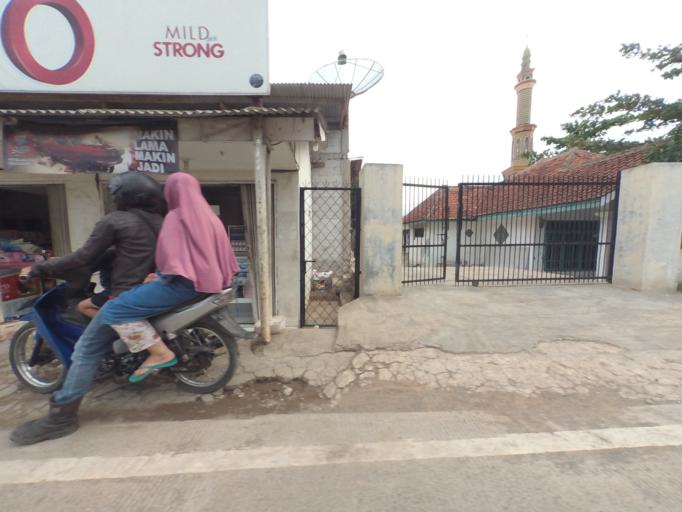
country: ID
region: West Java
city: Sidoger Lebak
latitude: -6.5650
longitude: 106.5866
